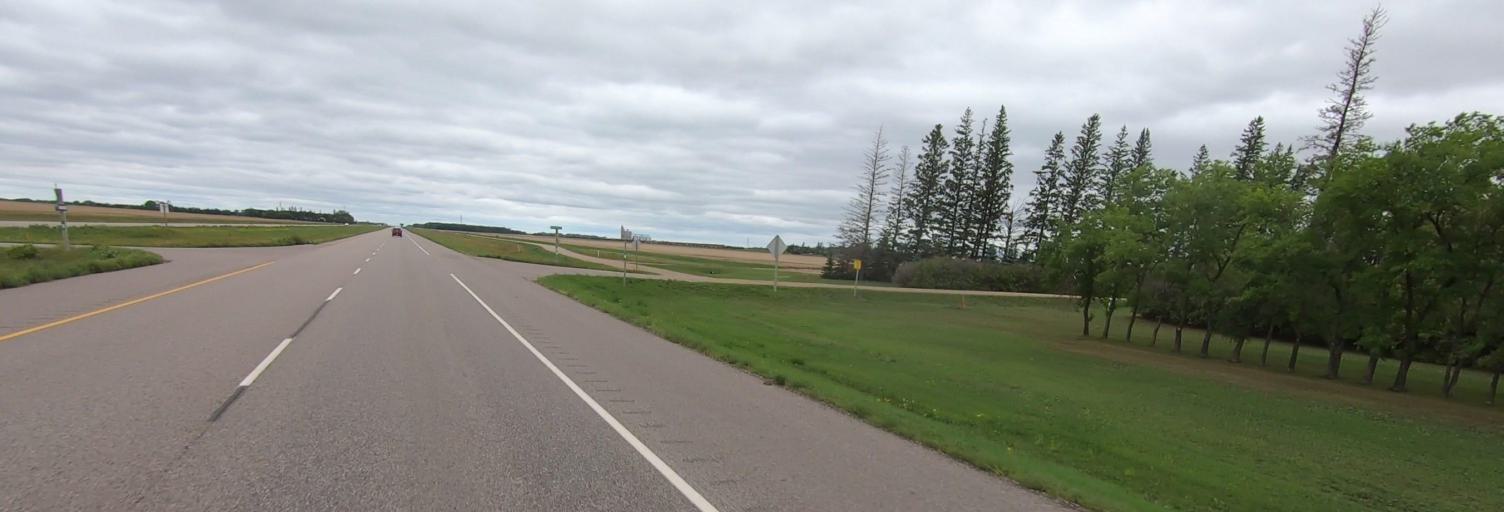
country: CA
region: Manitoba
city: Portage la Prairie
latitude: 49.9752
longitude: -98.5136
